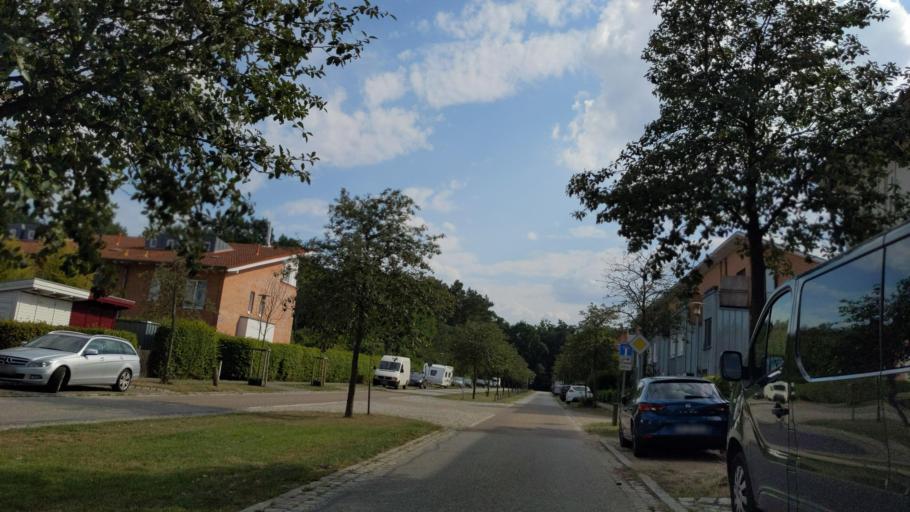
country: DE
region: Schleswig-Holstein
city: Gross Gronau
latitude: 53.8477
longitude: 10.7612
